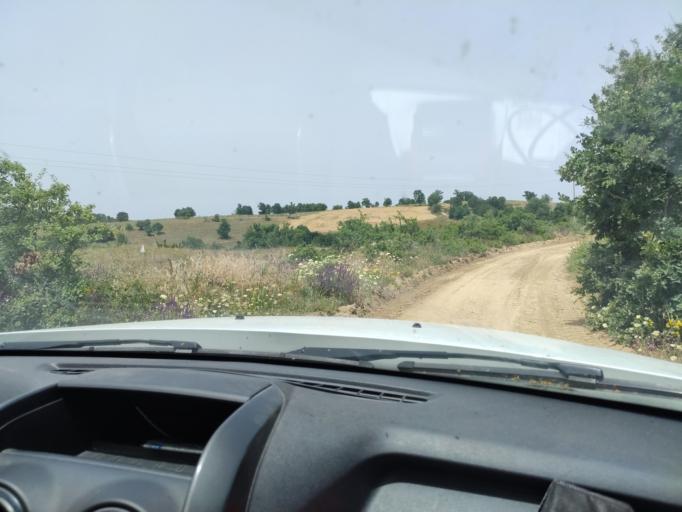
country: MK
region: Radovis
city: Radovish
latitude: 41.6747
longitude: 22.4036
